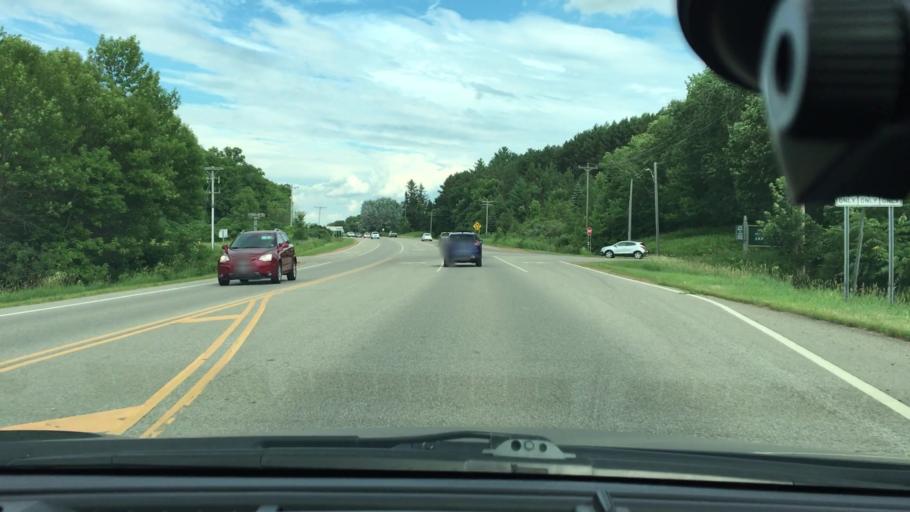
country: US
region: Minnesota
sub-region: Hennepin County
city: Shorewood
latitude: 44.8641
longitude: -93.6099
